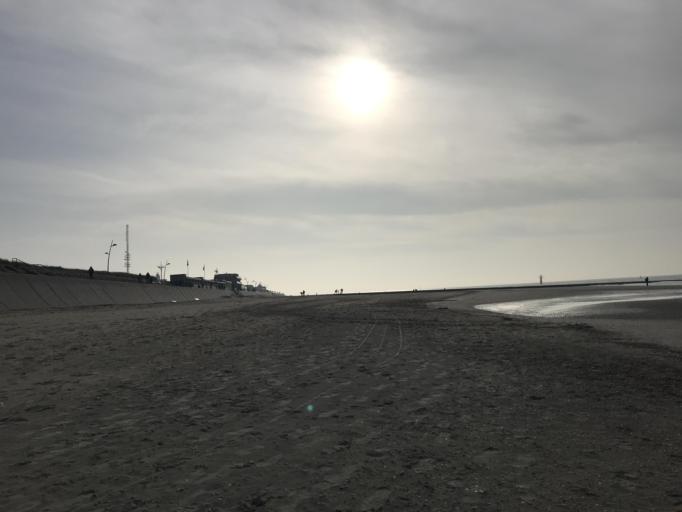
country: DE
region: Lower Saxony
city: Borkum
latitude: 53.5825
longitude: 6.6589
